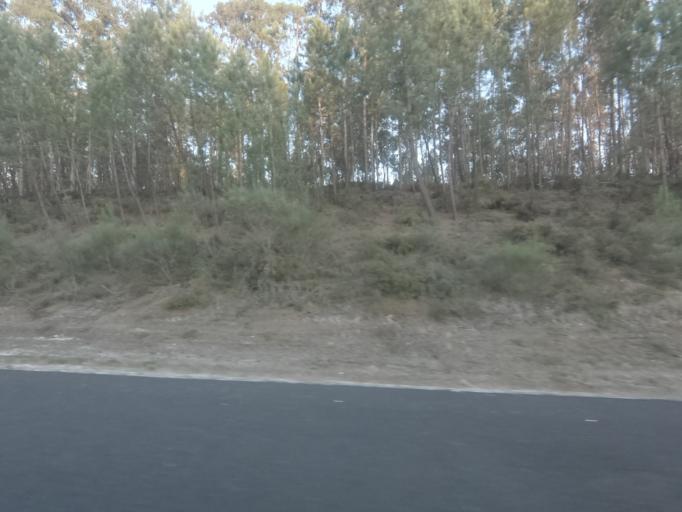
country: PT
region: Leiria
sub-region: Leiria
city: Caranguejeira
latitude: 39.7953
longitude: -8.7313
